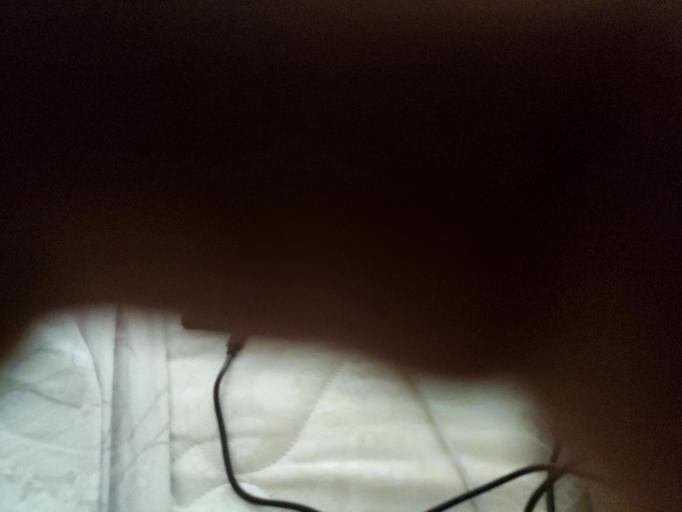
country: RU
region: Krasnodarskiy
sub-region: Sochi City
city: Krasnaya Polyana
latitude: 43.6787
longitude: 40.2758
